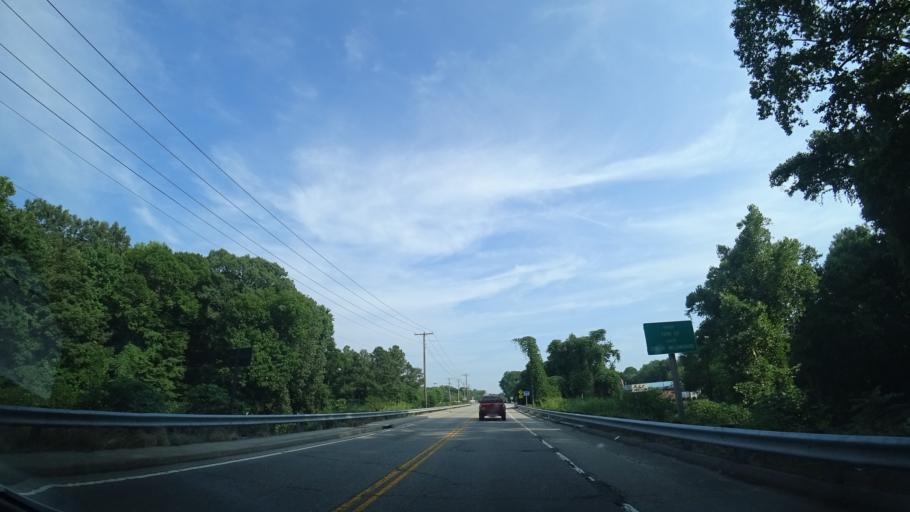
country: US
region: Virginia
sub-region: City of Williamsburg
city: Williamsburg
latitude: 37.2755
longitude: -76.6808
